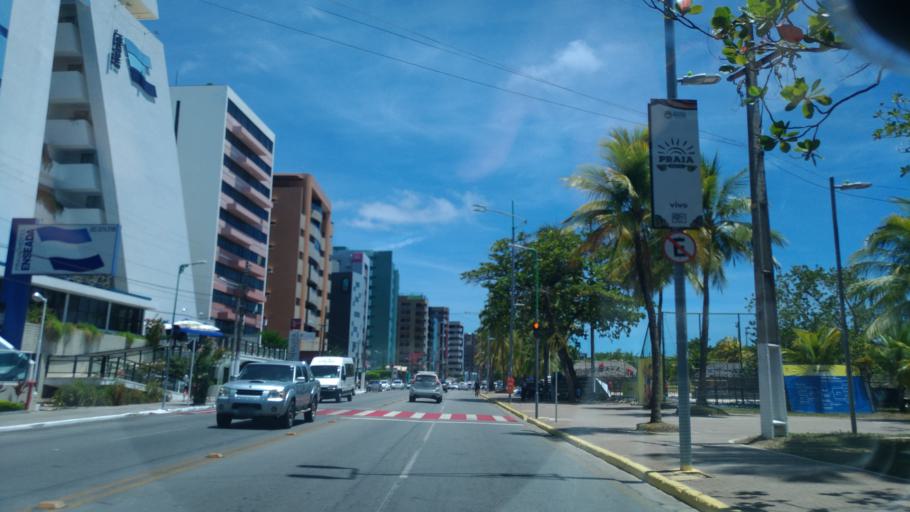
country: BR
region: Alagoas
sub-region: Maceio
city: Maceio
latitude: -9.6724
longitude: -35.7165
